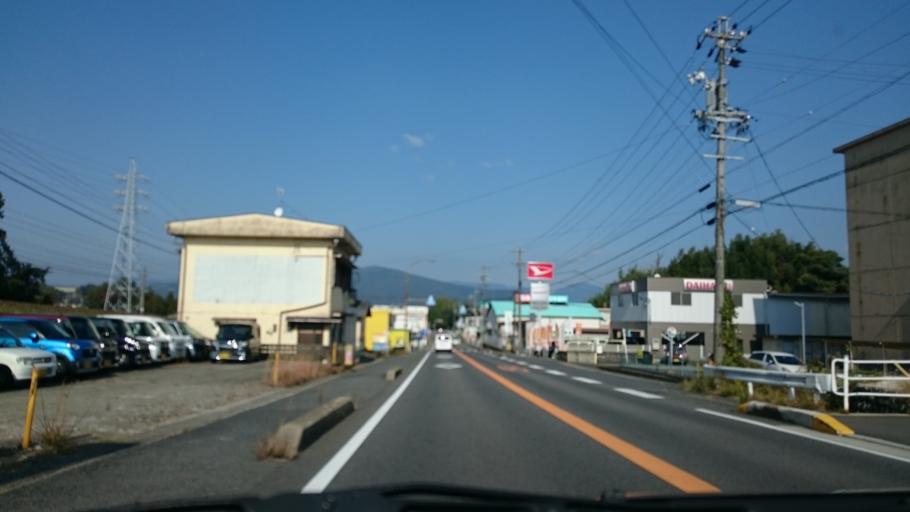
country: JP
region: Gifu
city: Nakatsugawa
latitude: 35.4824
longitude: 137.4860
